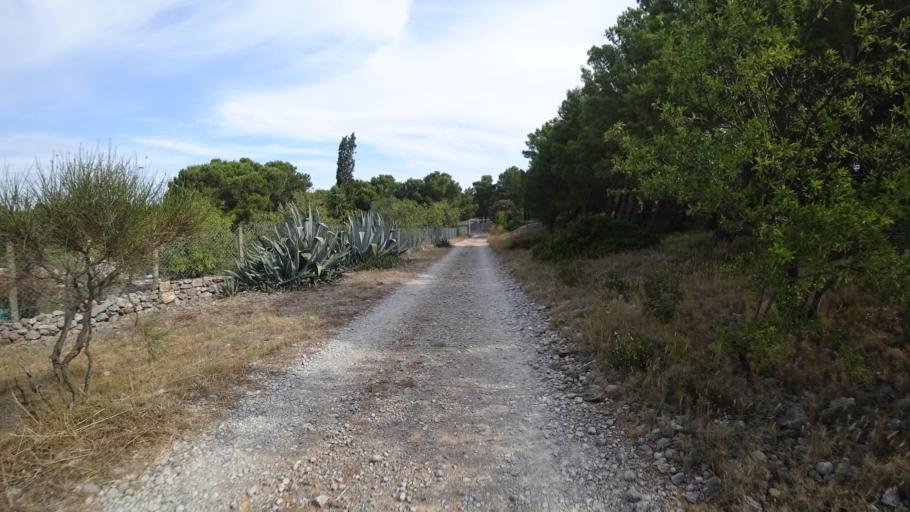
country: FR
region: Languedoc-Roussillon
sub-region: Departement de l'Aude
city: Leucate
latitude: 42.9003
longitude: 3.0325
